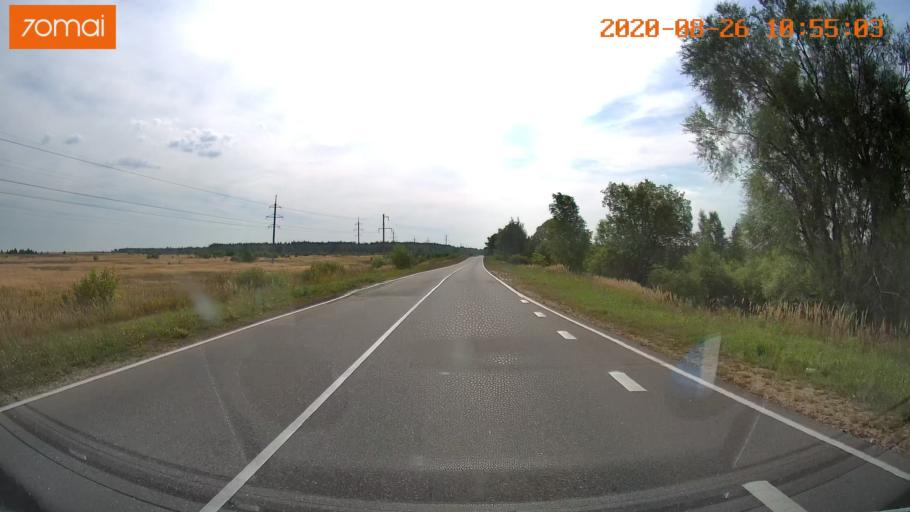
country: RU
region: Rjazan
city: Izhevskoye
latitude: 54.6223
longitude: 41.1706
